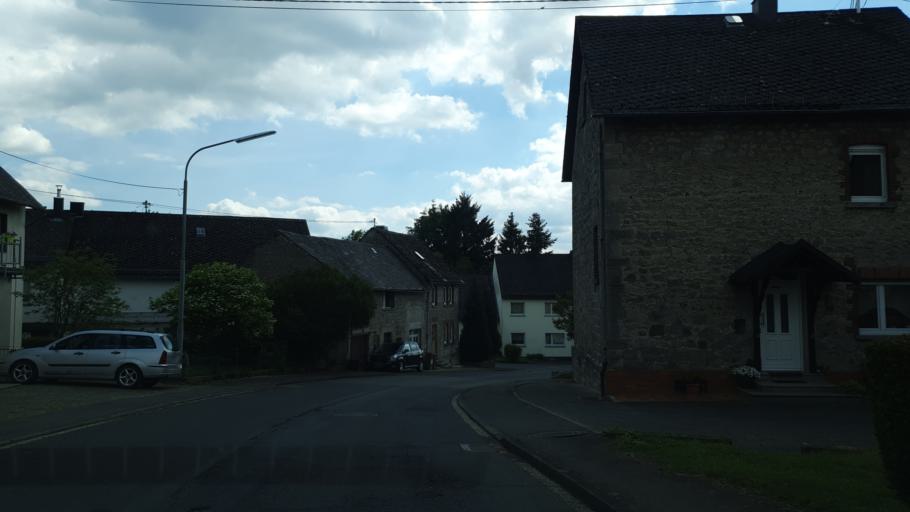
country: DE
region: Rheinland-Pfalz
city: Weidenhahn
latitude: 50.5465
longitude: 7.8398
